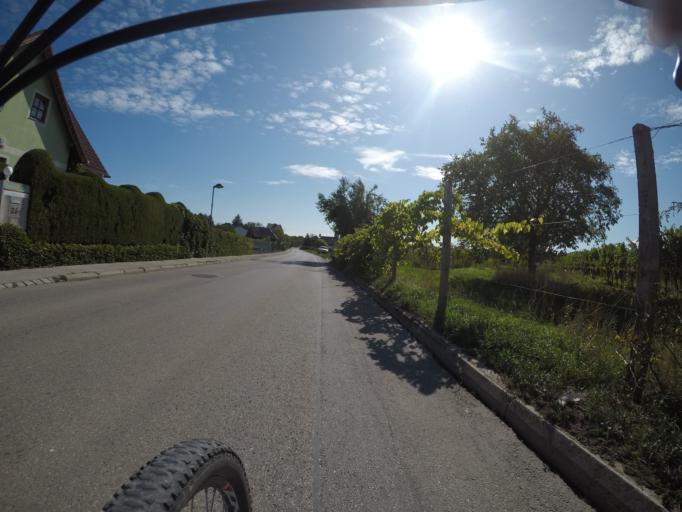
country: AT
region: Lower Austria
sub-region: Politischer Bezirk Modling
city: Maria Enzersdorf
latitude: 48.0996
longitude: 16.2911
